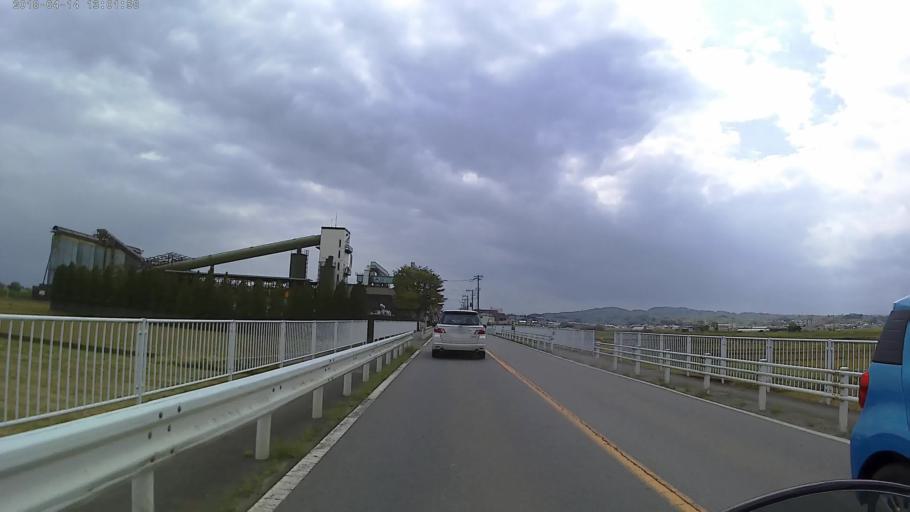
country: JP
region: Kanagawa
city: Isehara
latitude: 35.3701
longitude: 139.2988
